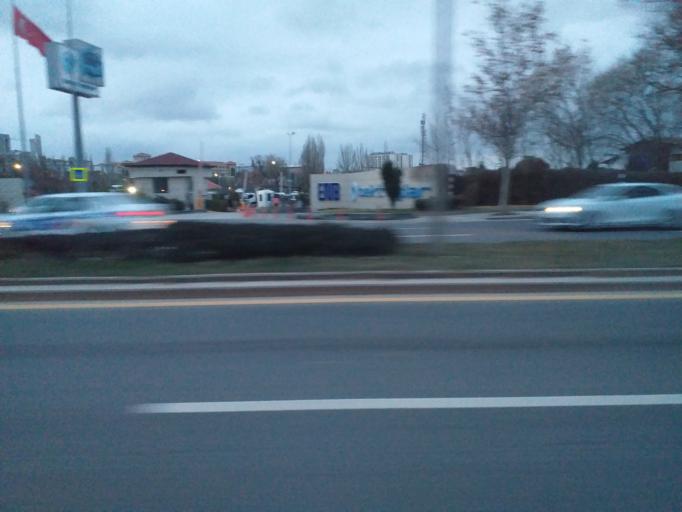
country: TR
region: Ankara
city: Ankara
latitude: 39.9485
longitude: 32.8273
